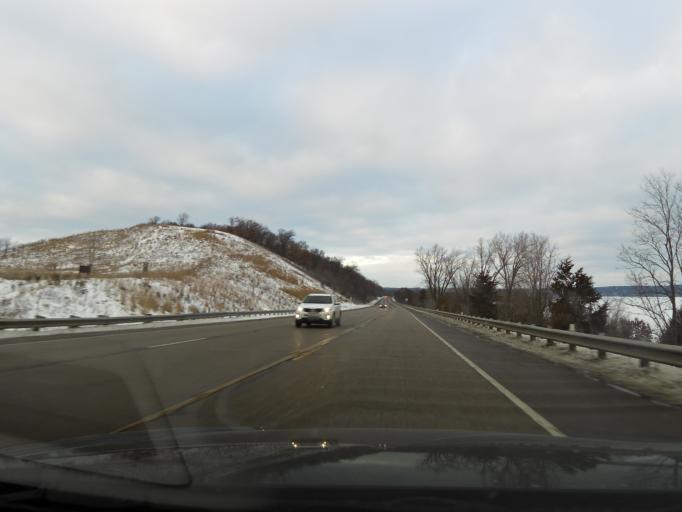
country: US
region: Wisconsin
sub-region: Saint Croix County
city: North Hudson
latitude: 44.9943
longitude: -92.7778
